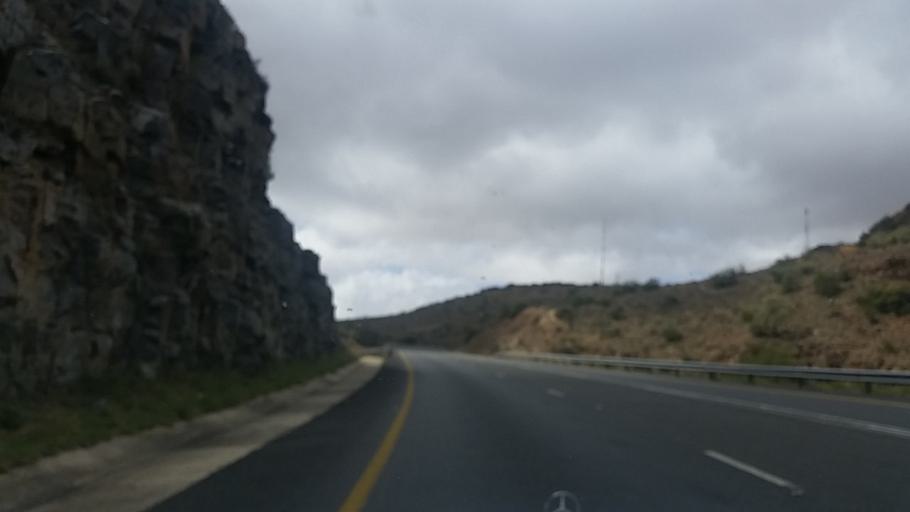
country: ZA
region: Eastern Cape
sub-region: Cacadu District Municipality
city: Graaff-Reinet
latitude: -31.9666
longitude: 24.7218
